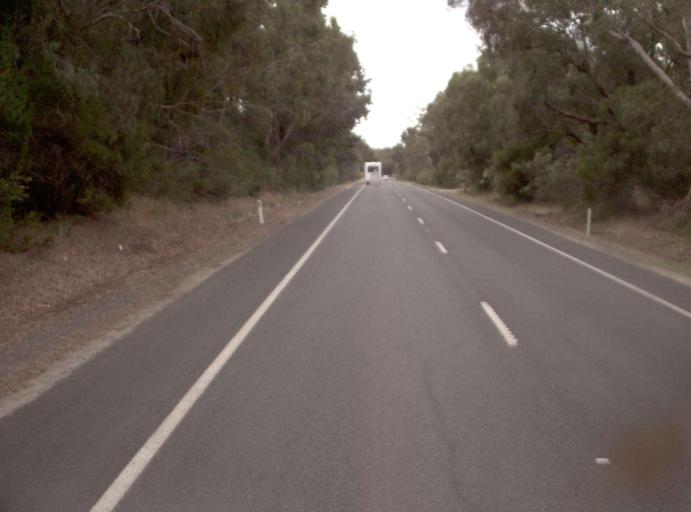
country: AU
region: Victoria
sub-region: Wellington
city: Sale
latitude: -38.1890
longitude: 147.0800
